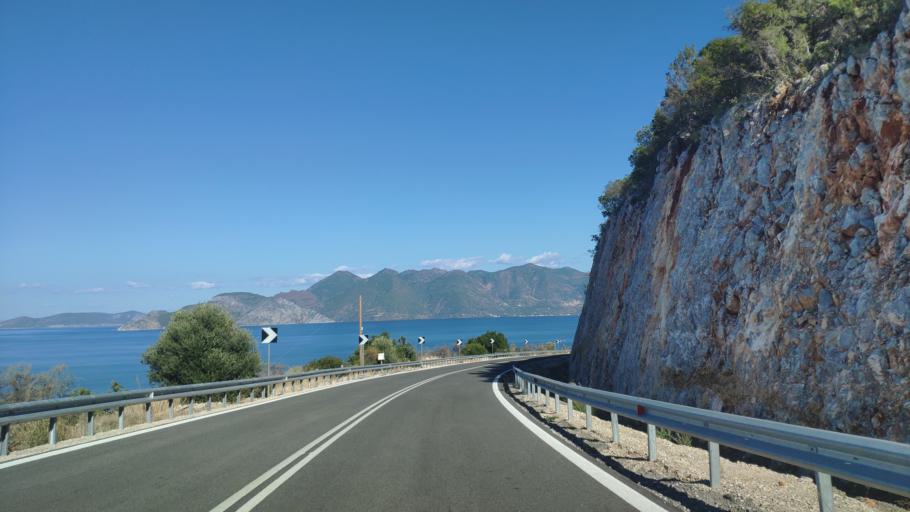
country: GR
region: Peloponnese
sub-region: Nomos Argolidos
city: Didyma
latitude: 37.5545
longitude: 23.2687
